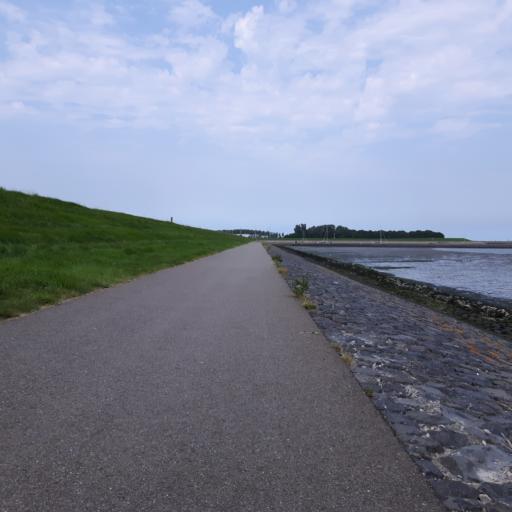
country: NL
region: Zeeland
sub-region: Gemeente Goes
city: Goes
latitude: 51.5334
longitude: 3.9316
